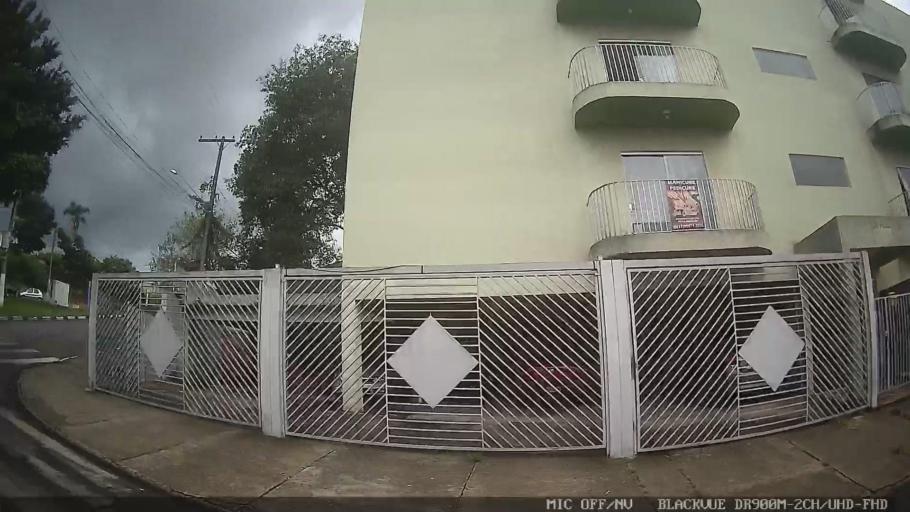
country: BR
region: Sao Paulo
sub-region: Atibaia
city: Atibaia
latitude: -23.1385
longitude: -46.5814
